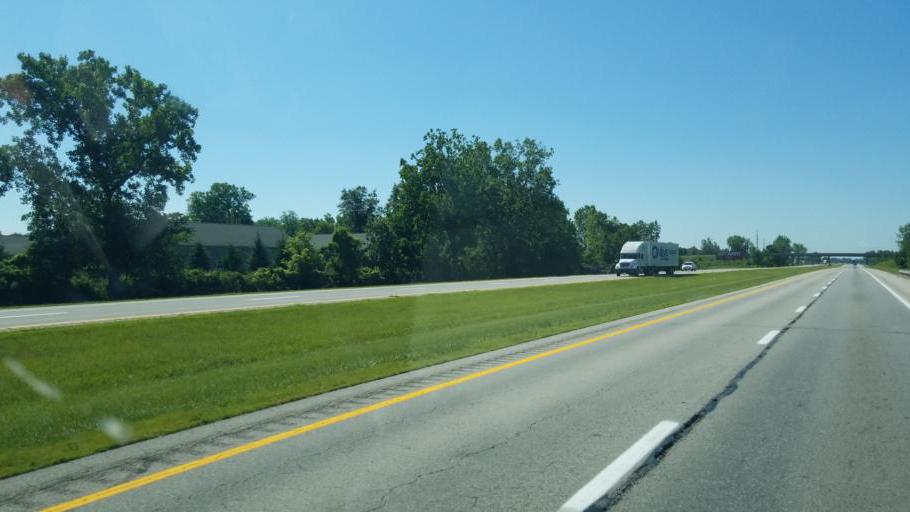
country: US
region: Ohio
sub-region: Marion County
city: Marion
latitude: 40.6340
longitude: -83.0979
